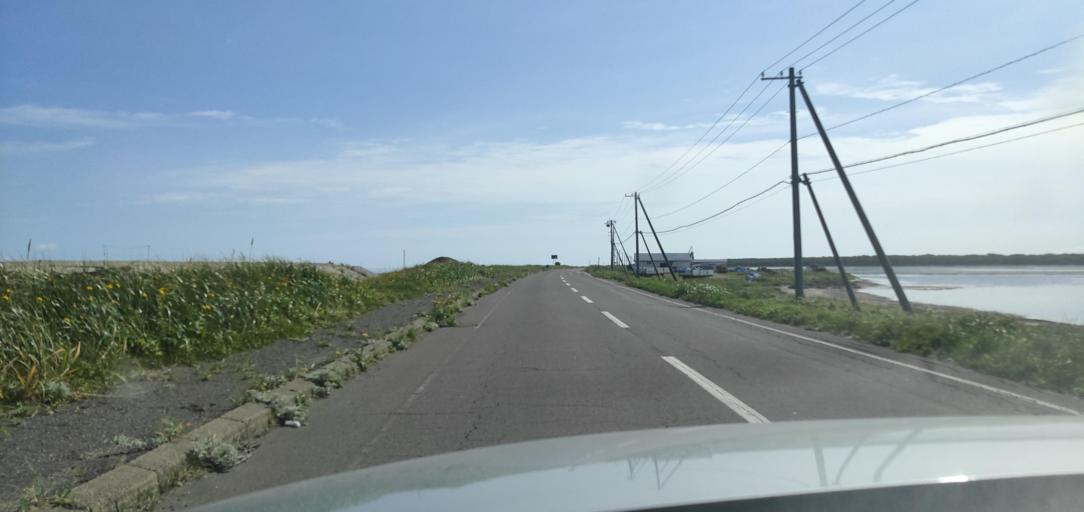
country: JP
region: Hokkaido
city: Shibetsu
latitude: 43.6131
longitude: 145.2534
